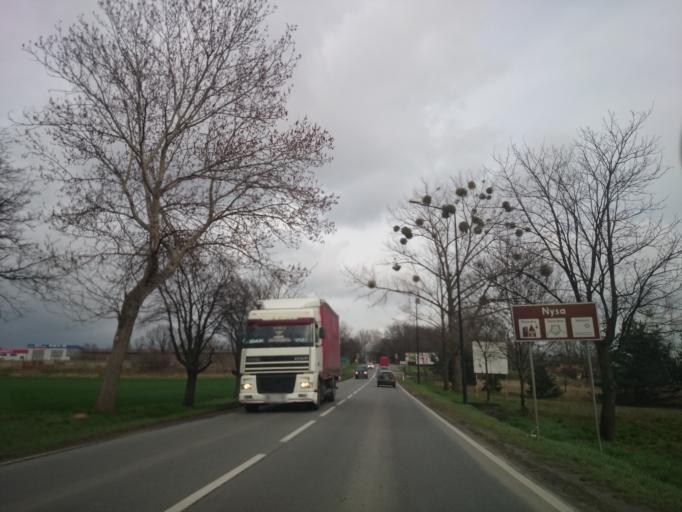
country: PL
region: Opole Voivodeship
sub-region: Powiat nyski
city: Nysa
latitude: 50.4790
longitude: 17.2917
